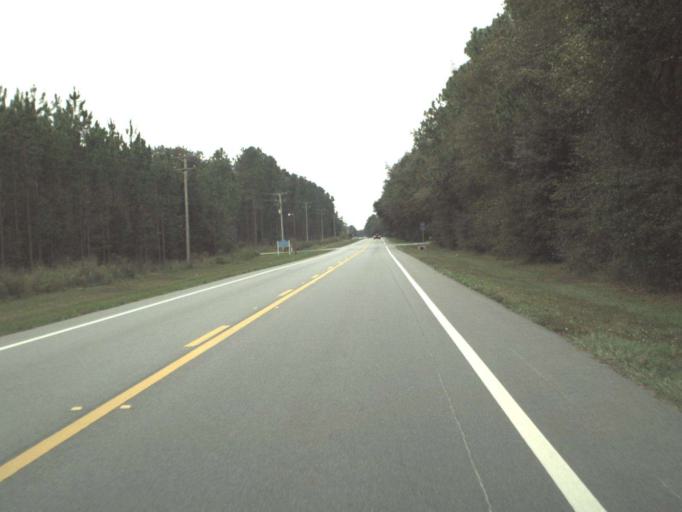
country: US
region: Florida
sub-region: Jackson County
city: Sneads
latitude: 30.7323
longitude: -85.0200
